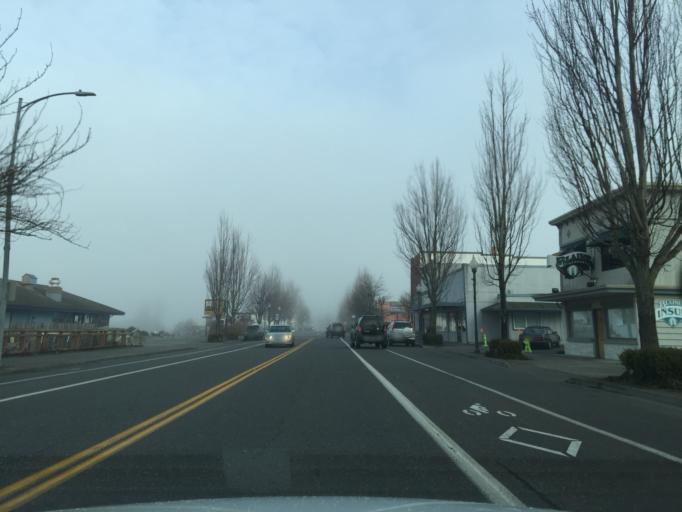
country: US
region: Washington
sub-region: Whatcom County
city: Blaine
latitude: 48.9923
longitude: -122.7516
